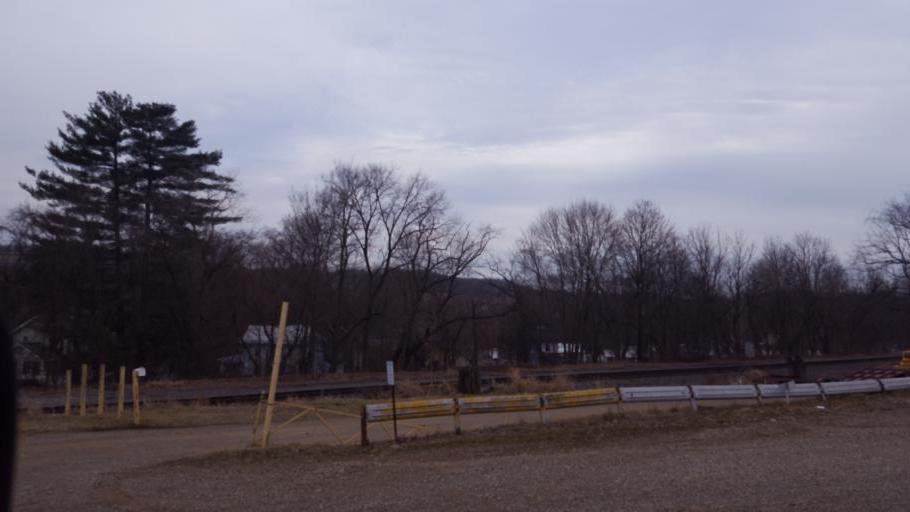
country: US
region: Ohio
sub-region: Ashland County
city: Loudonville
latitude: 40.6406
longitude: -82.2365
